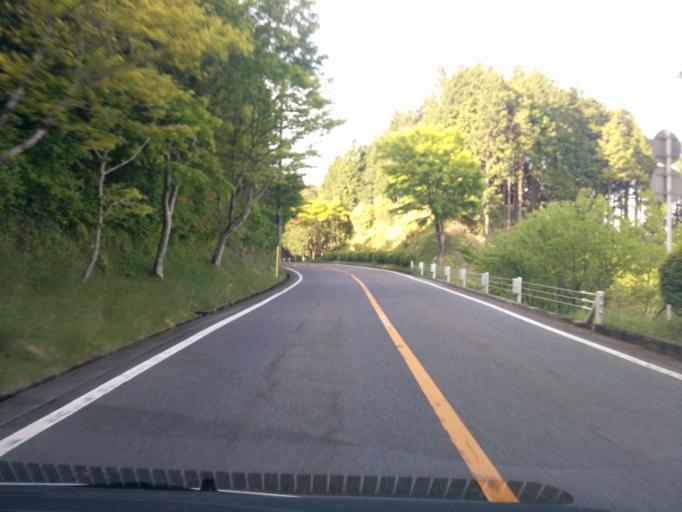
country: JP
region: Shiga Prefecture
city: Otsu-shi
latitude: 35.0836
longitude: 135.8392
